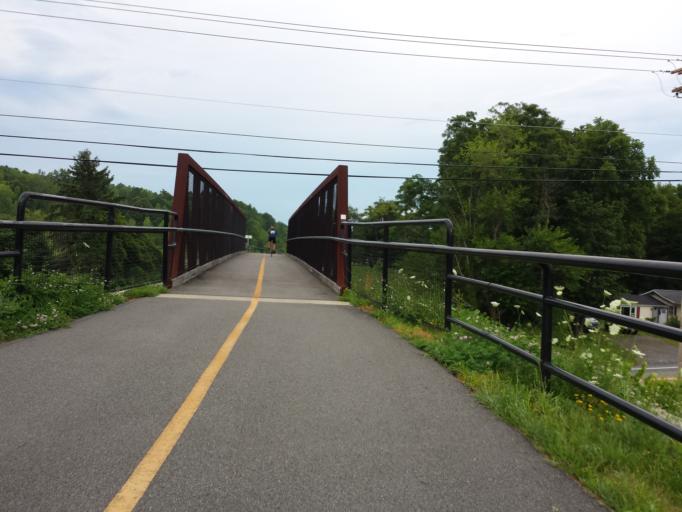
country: US
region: New York
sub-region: Dutchess County
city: Red Oaks Mill
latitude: 41.6579
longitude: -73.8548
